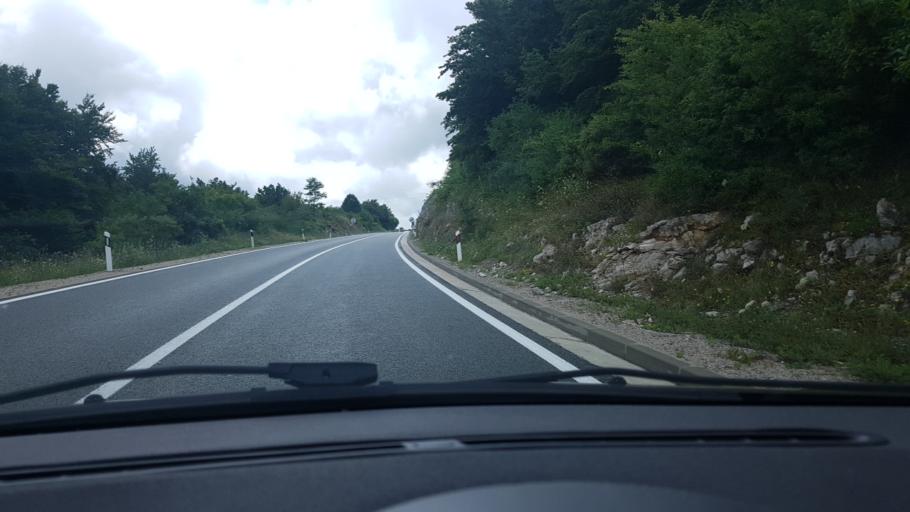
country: HR
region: Licko-Senjska
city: Jezerce
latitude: 44.8599
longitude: 15.6960
